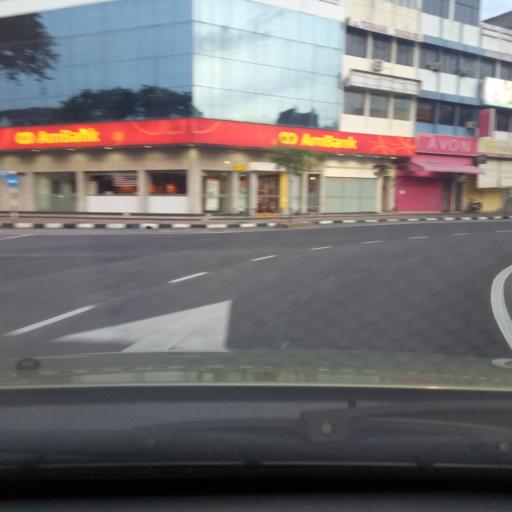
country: MY
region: Kedah
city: Alor Setar
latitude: 6.1200
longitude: 100.3693
